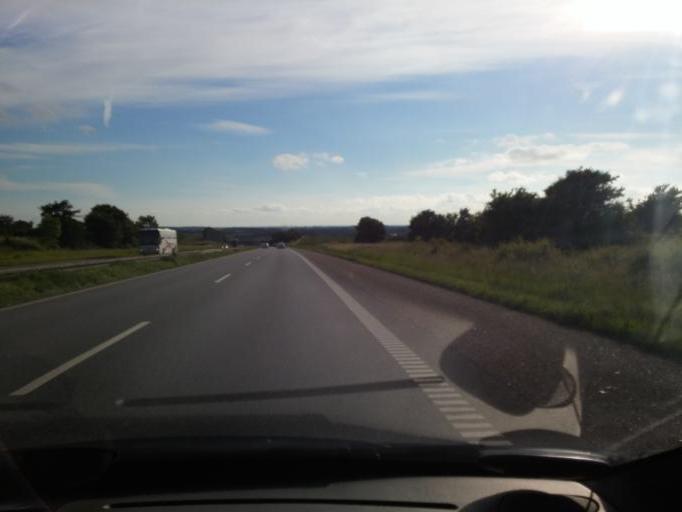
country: DK
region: Zealand
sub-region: Slagelse Kommune
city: Forlev
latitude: 55.3789
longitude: 11.3173
